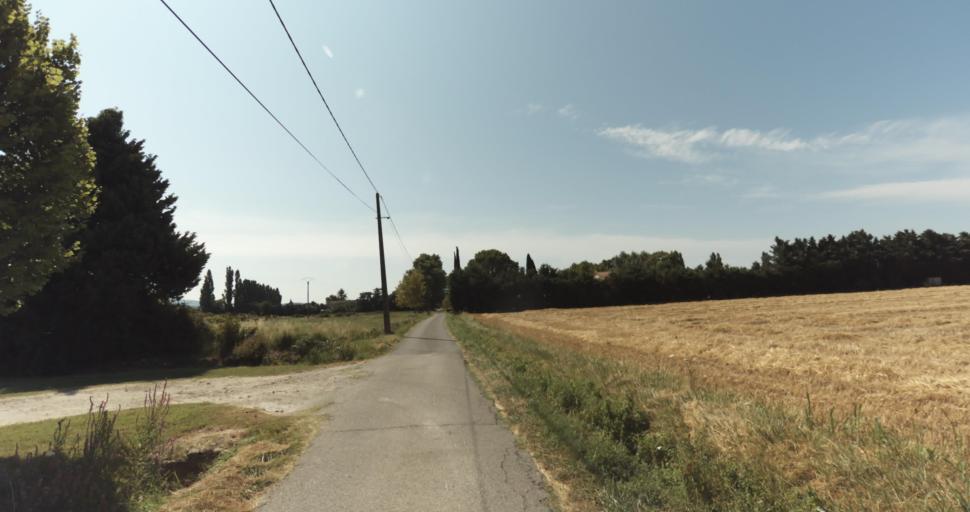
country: FR
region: Provence-Alpes-Cote d'Azur
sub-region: Departement du Vaucluse
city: Monteux
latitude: 44.0173
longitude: 4.9999
